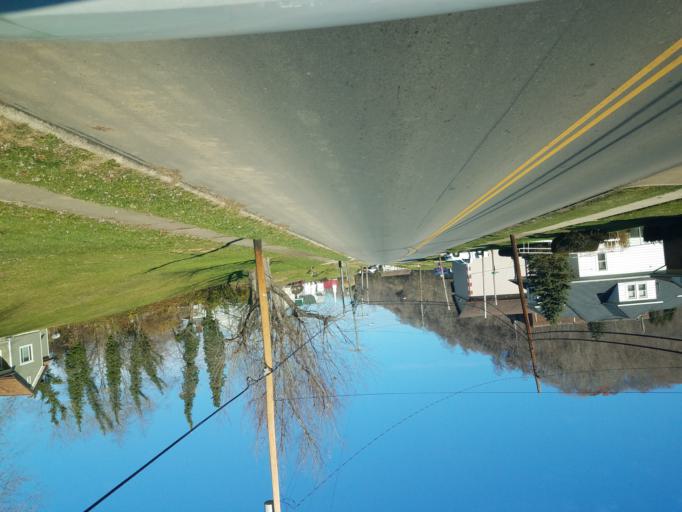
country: US
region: Ohio
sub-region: Scioto County
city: New Boston
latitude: 38.7625
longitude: -82.9348
